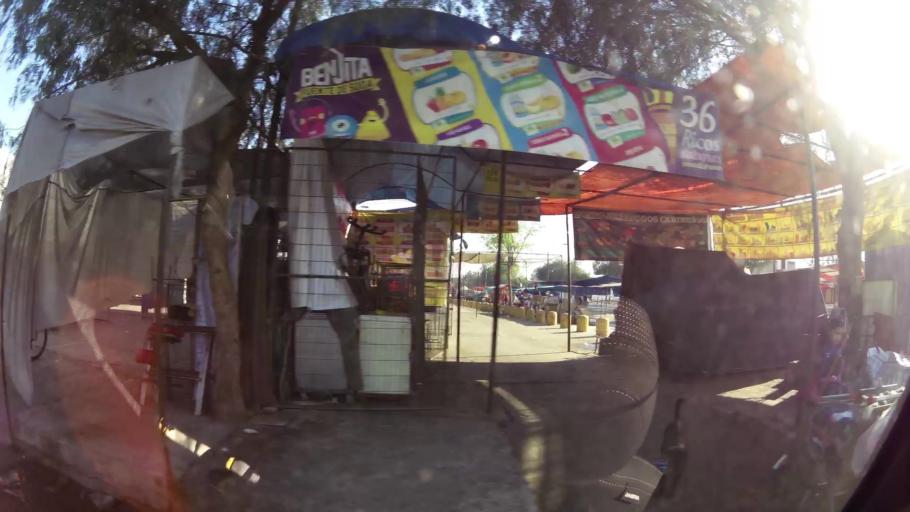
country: CL
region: Santiago Metropolitan
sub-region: Provincia de Santiago
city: Lo Prado
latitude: -33.4411
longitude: -70.7408
